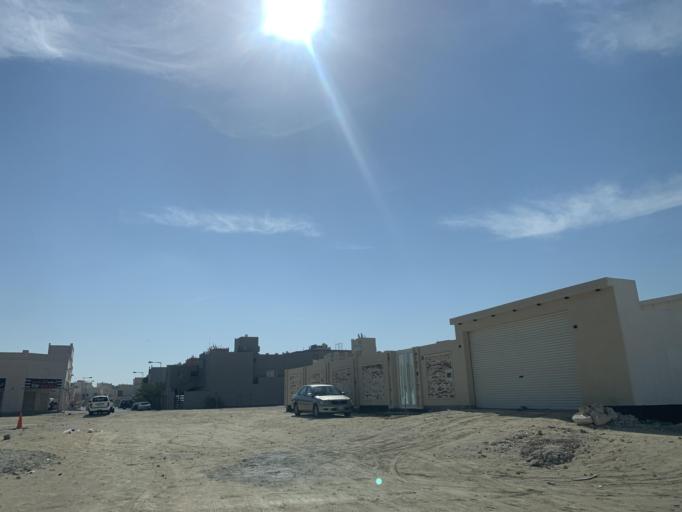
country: BH
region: Central Governorate
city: Madinat Hamad
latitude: 26.1155
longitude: 50.4874
